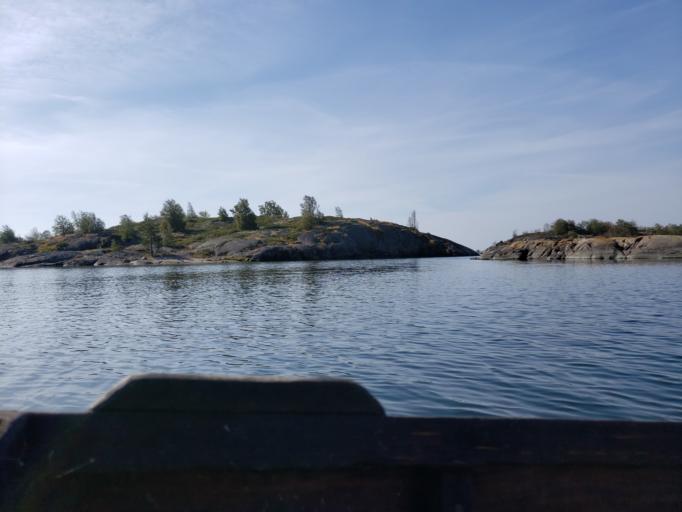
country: FI
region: Varsinais-Suomi
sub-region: Aboland-Turunmaa
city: Dragsfjaerd
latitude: 59.8547
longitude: 22.2140
